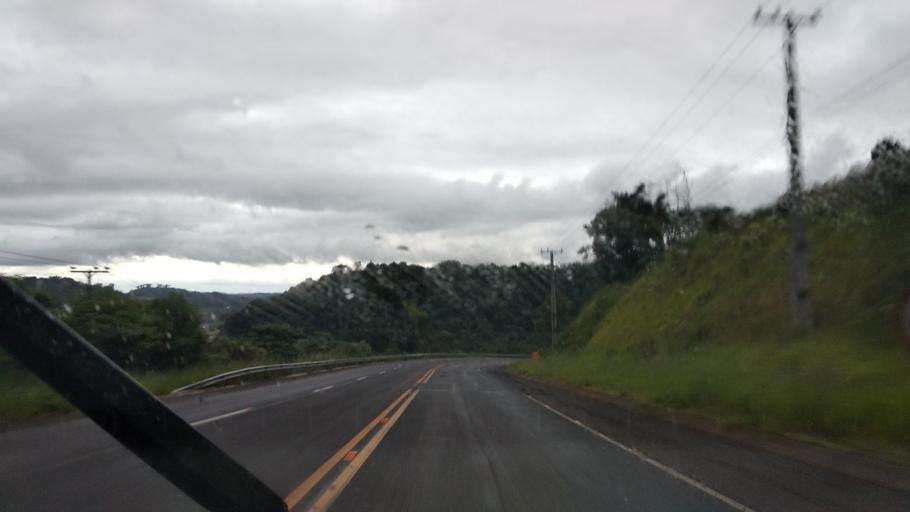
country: BR
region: Santa Catarina
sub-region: Videira
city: Videira
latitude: -27.0521
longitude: -51.1762
